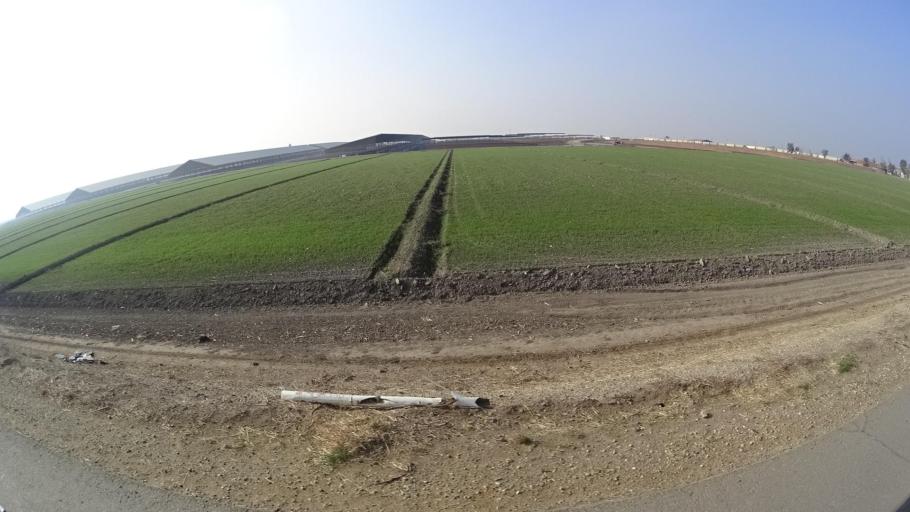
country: US
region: California
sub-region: Kern County
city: Greenfield
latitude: 35.1766
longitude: -119.1100
